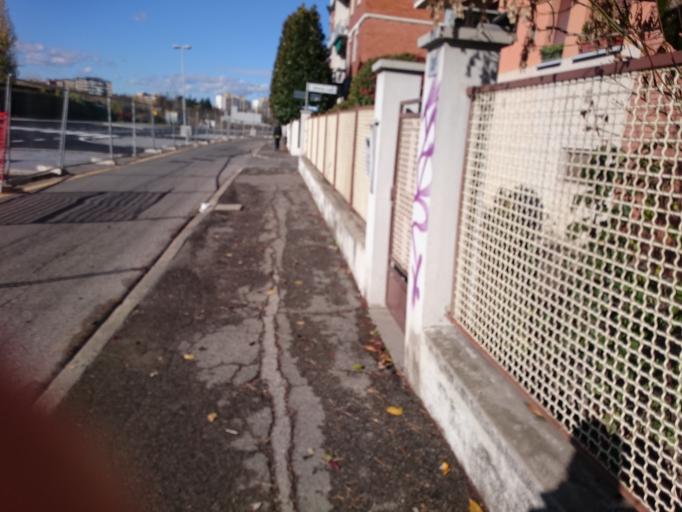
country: IT
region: Emilia-Romagna
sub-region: Provincia di Bologna
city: Bologna
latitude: 44.5142
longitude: 11.3387
